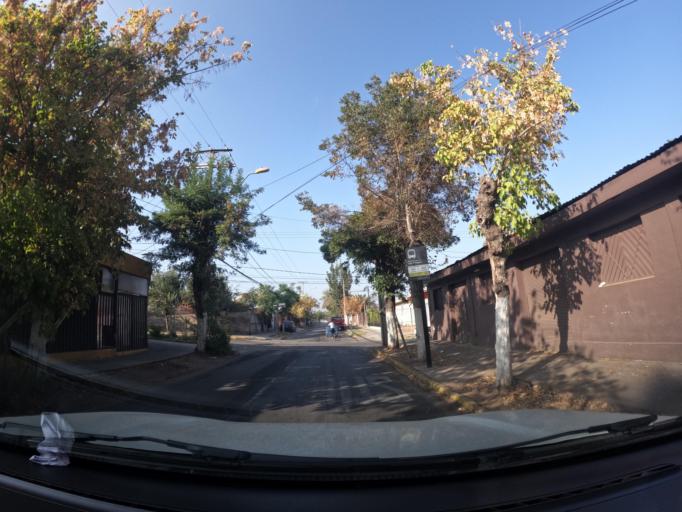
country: CL
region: Santiago Metropolitan
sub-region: Provincia de Santiago
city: Villa Presidente Frei, Nunoa, Santiago, Chile
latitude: -33.4692
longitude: -70.5380
